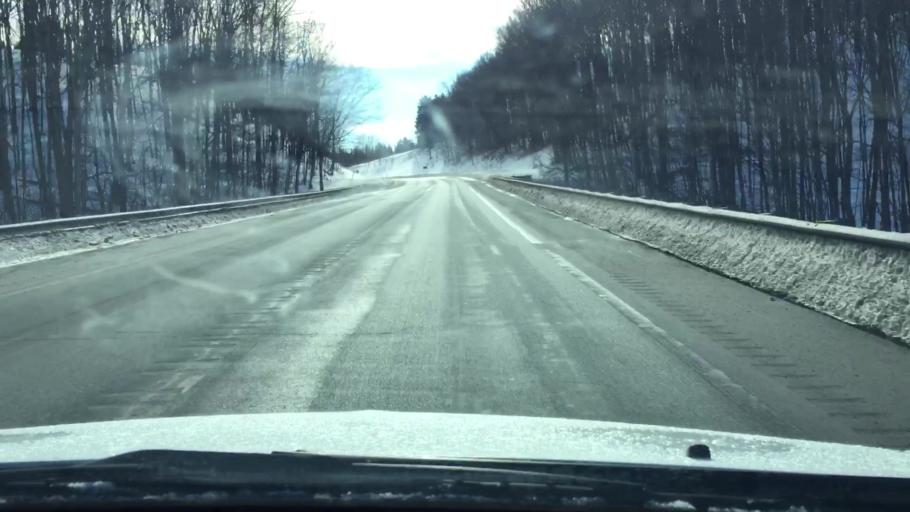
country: US
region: Michigan
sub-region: Antrim County
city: Mancelona
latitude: 44.9551
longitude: -85.0513
